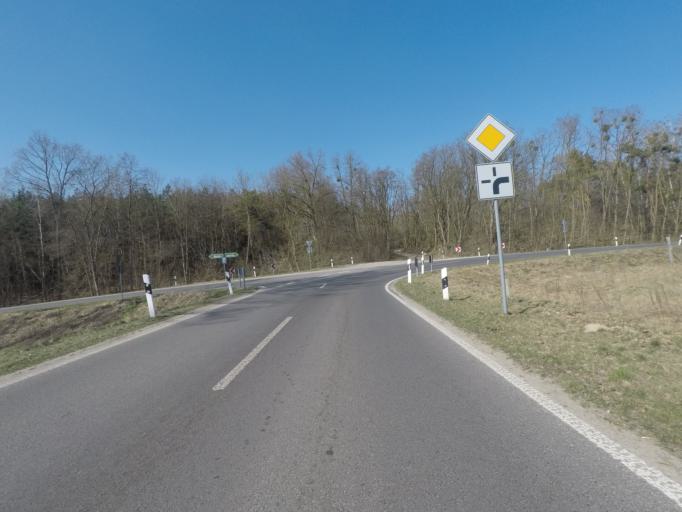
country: DE
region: Brandenburg
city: Marienwerder
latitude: 52.8598
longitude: 13.6836
